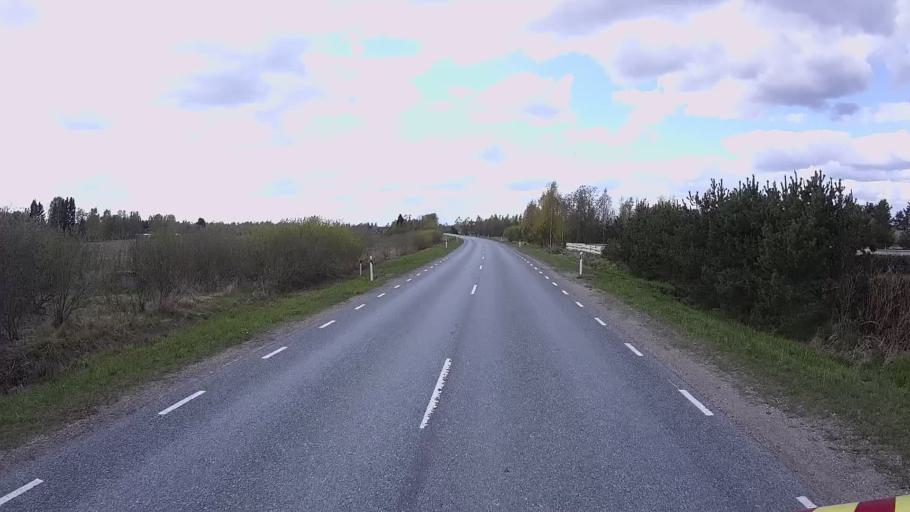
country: EE
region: Jogevamaa
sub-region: Mustvee linn
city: Mustvee
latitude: 58.7836
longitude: 26.9715
